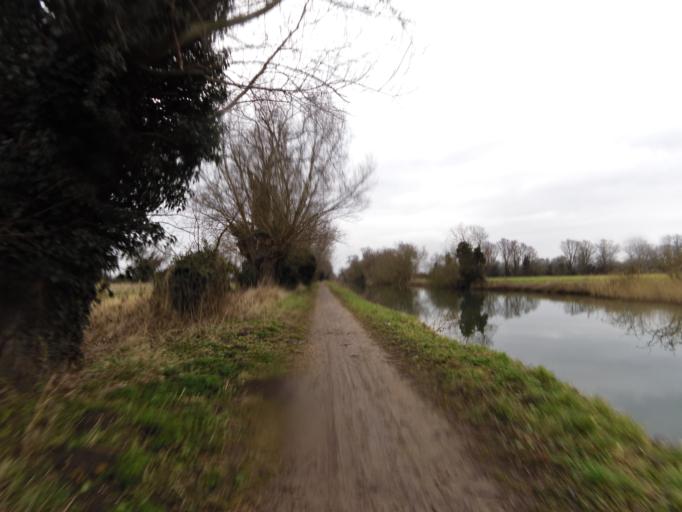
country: GB
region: England
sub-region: Cambridgeshire
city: Waterbeach
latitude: 52.2510
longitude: 0.1865
